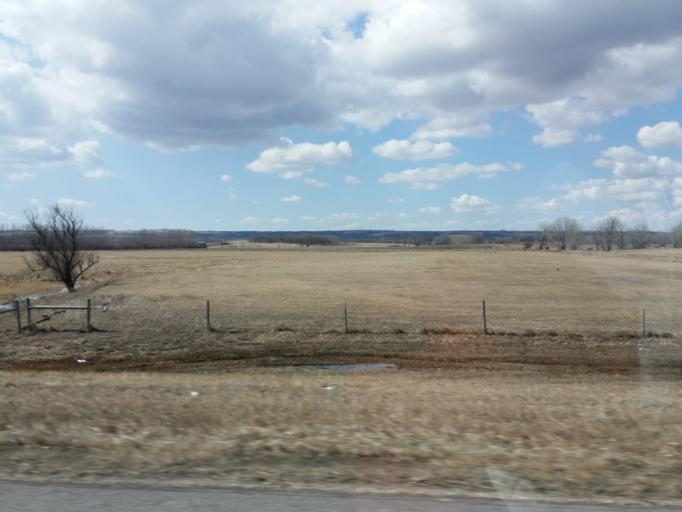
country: US
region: South Dakota
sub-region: Roberts County
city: Sisseton
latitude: 45.5288
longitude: -96.9896
